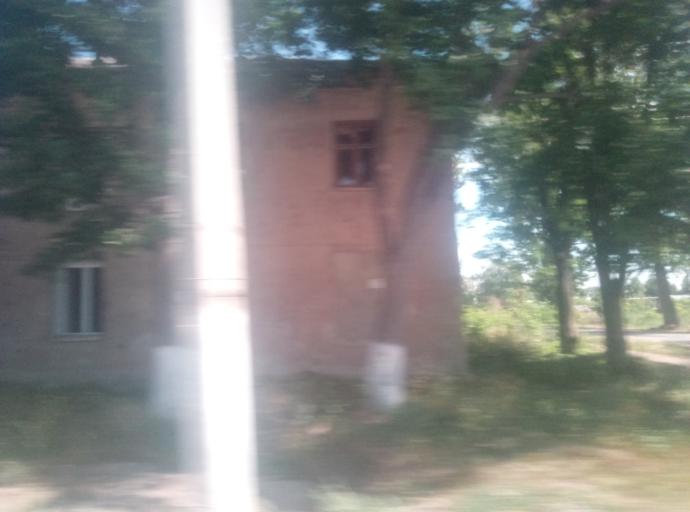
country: RU
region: Tula
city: Kireyevsk
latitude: 53.9251
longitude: 37.9229
